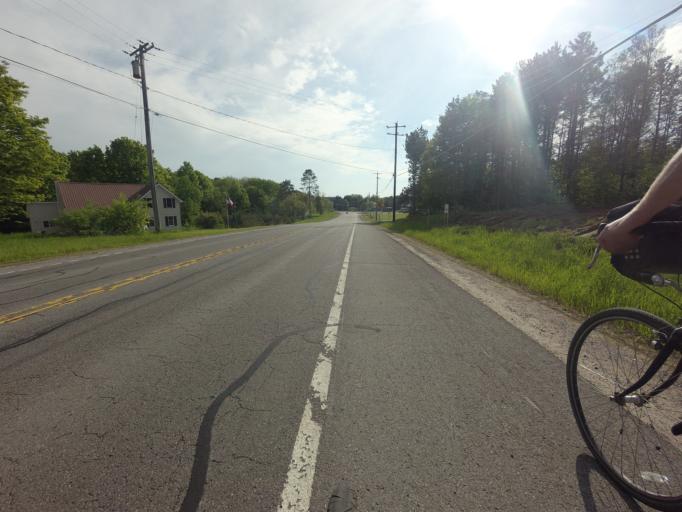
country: US
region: New York
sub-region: St. Lawrence County
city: Gouverneur
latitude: 44.1641
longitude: -75.3098
